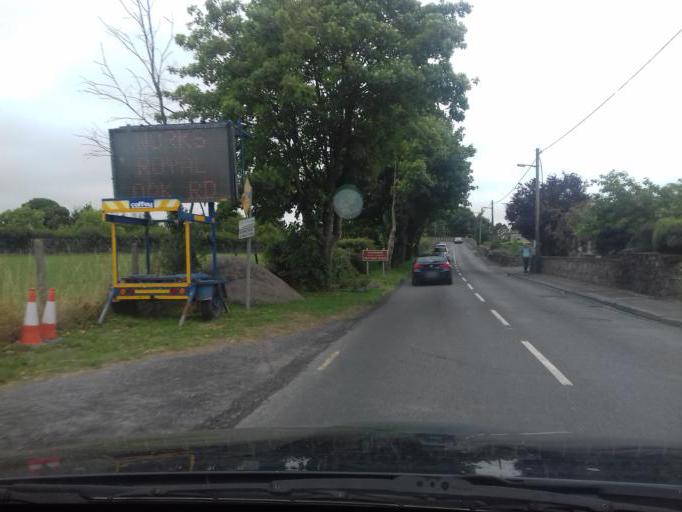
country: IE
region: Leinster
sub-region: County Carlow
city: Bagenalstown
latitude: 52.6958
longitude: -6.9582
